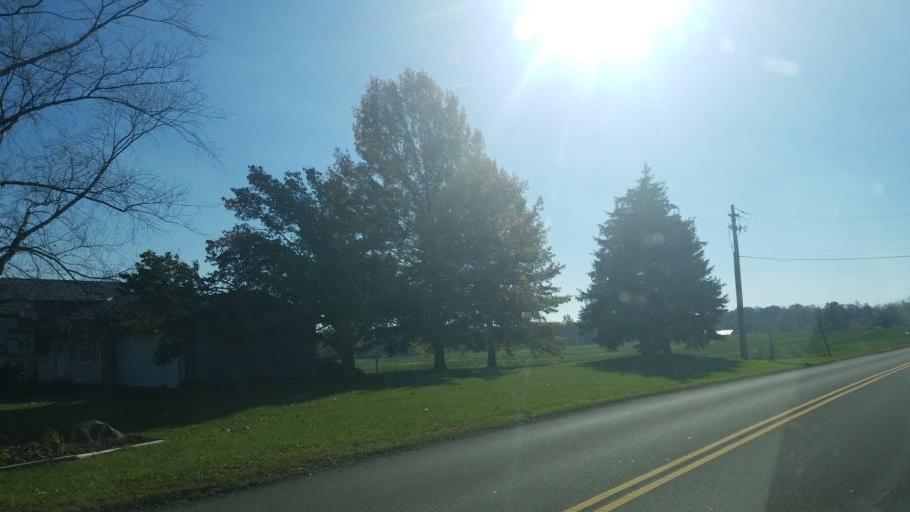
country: US
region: Ohio
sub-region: Ashland County
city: Ashland
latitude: 40.8367
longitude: -82.3336
